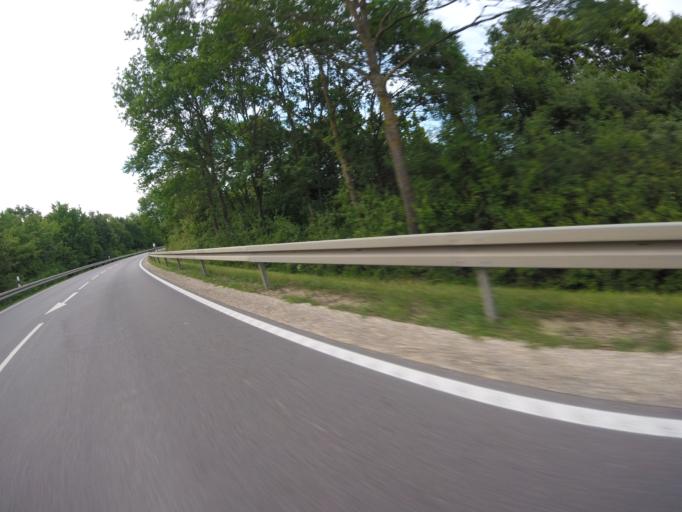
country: DE
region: Bavaria
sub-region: Upper Bavaria
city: Reichertshausen
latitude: 48.4596
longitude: 11.5148
